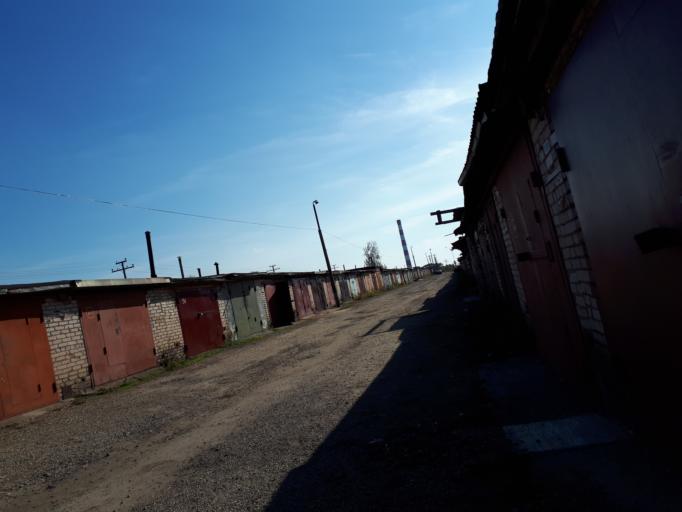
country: BY
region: Vitebsk
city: Vitebsk
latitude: 55.1656
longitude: 30.2448
